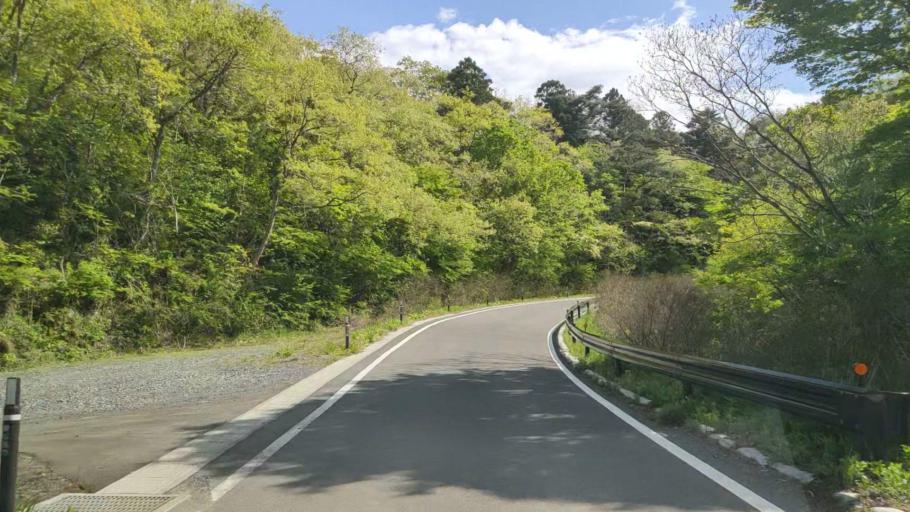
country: JP
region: Miyagi
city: Matsushima
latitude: 38.3407
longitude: 141.1557
